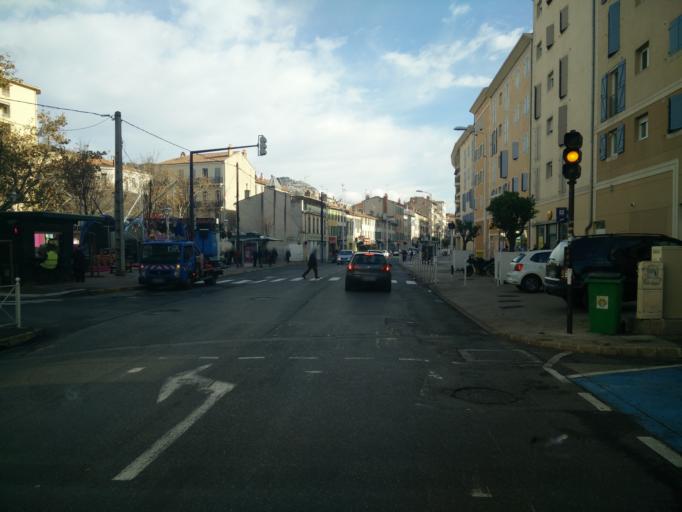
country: FR
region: Provence-Alpes-Cote d'Azur
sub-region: Departement du Var
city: Toulon
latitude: 43.1285
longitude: 5.9096
